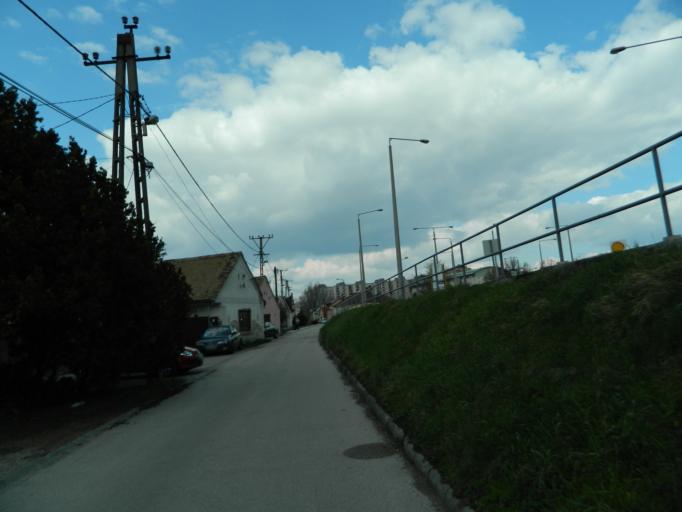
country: HU
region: Fejer
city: Szekesfehervar
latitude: 47.1808
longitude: 18.4064
